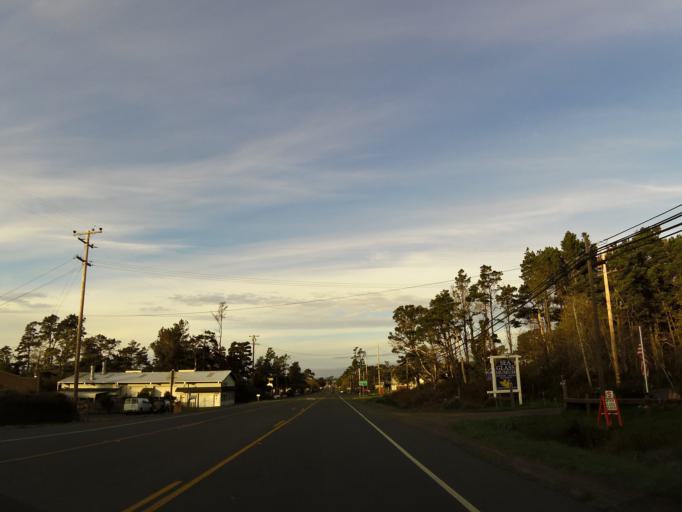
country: US
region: California
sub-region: Mendocino County
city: Fort Bragg
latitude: 39.4024
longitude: -123.8090
